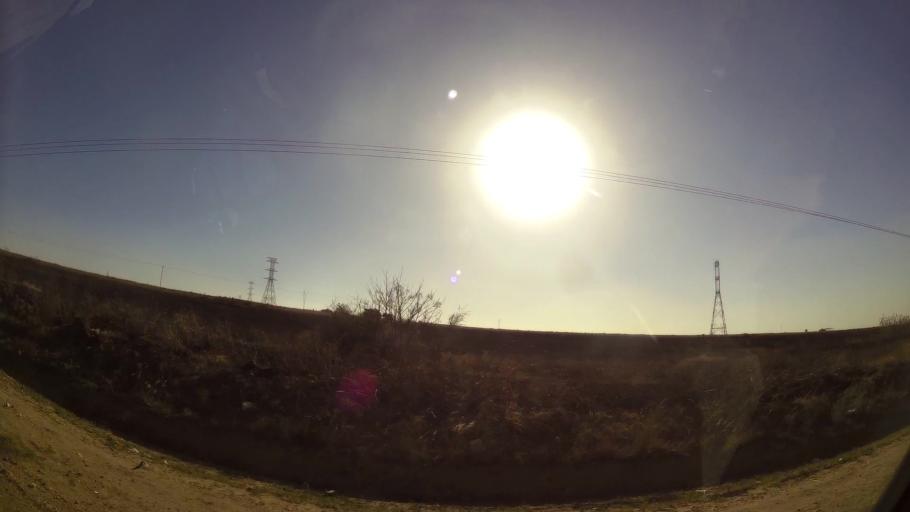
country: ZA
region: Gauteng
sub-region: City of Johannesburg Metropolitan Municipality
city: Diepsloot
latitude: -25.9655
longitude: 27.9533
